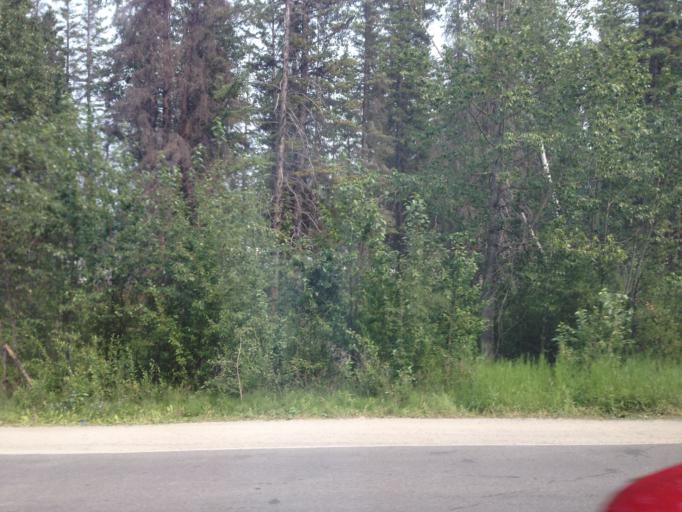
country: CA
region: Alberta
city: Banff
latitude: 51.1820
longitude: -115.5796
